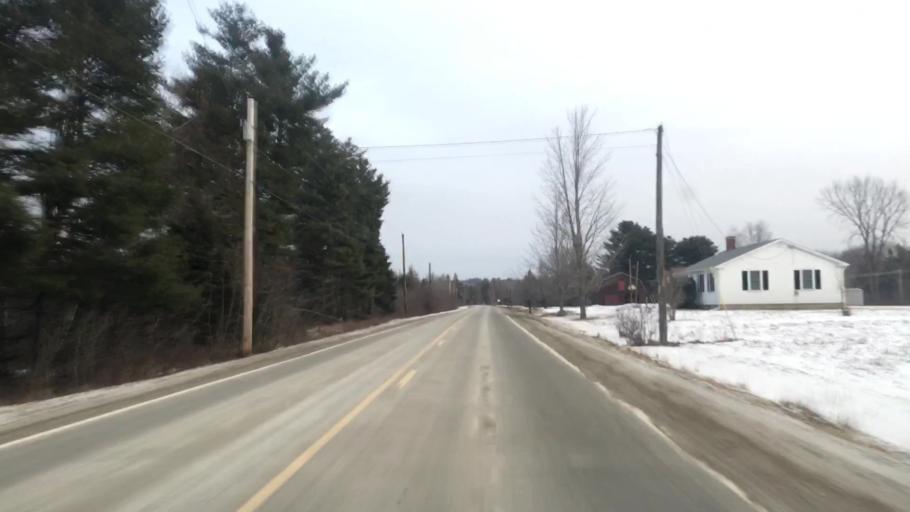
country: US
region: Maine
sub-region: Hancock County
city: Franklin
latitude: 44.6911
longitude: -68.3480
